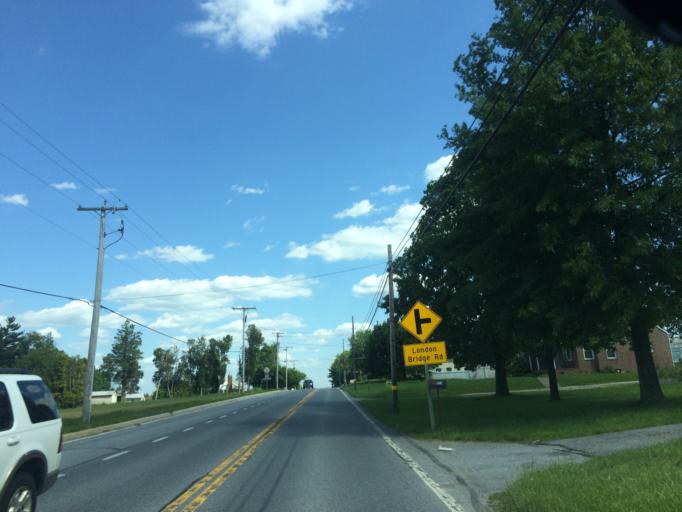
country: US
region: Maryland
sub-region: Carroll County
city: Eldersburg
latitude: 39.4753
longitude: -76.9502
